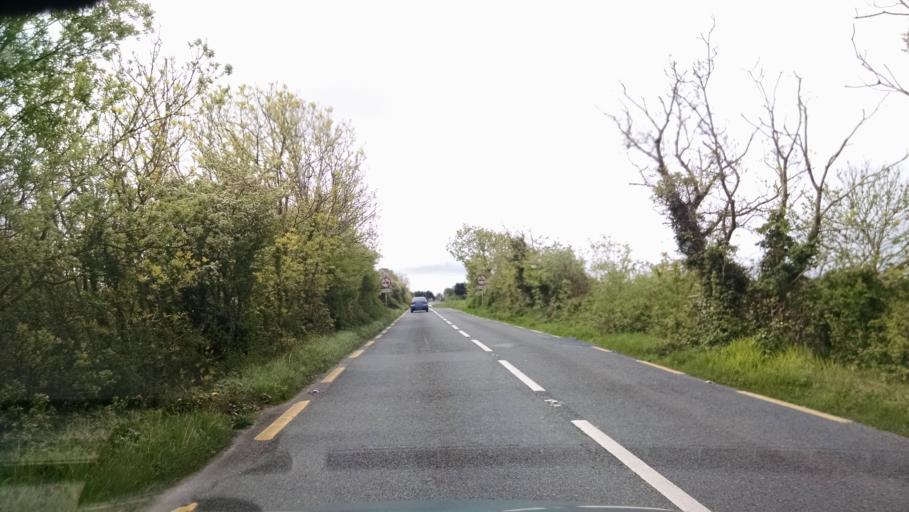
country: IE
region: Connaught
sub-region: County Galway
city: Claregalway
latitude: 53.3815
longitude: -9.0162
